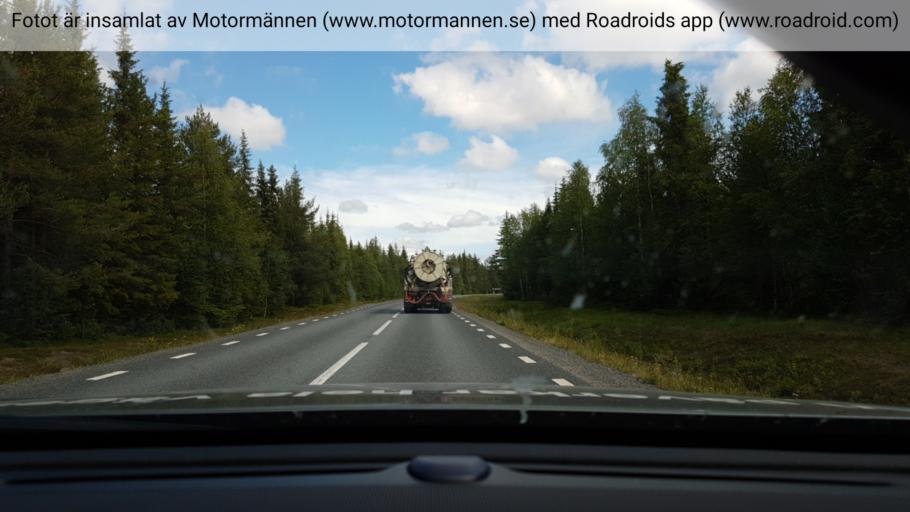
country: SE
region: Vaesterbotten
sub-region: Sorsele Kommun
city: Sorsele
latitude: 65.5583
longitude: 17.8363
